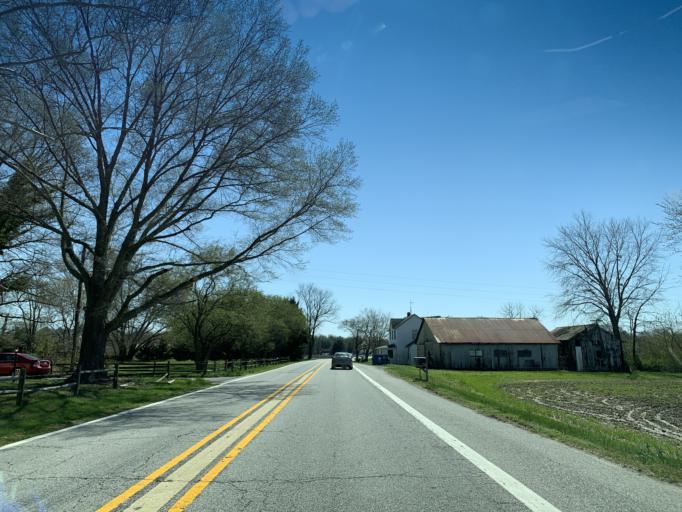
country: US
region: Maryland
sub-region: Queen Anne's County
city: Centreville
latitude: 38.9792
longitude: -76.0117
